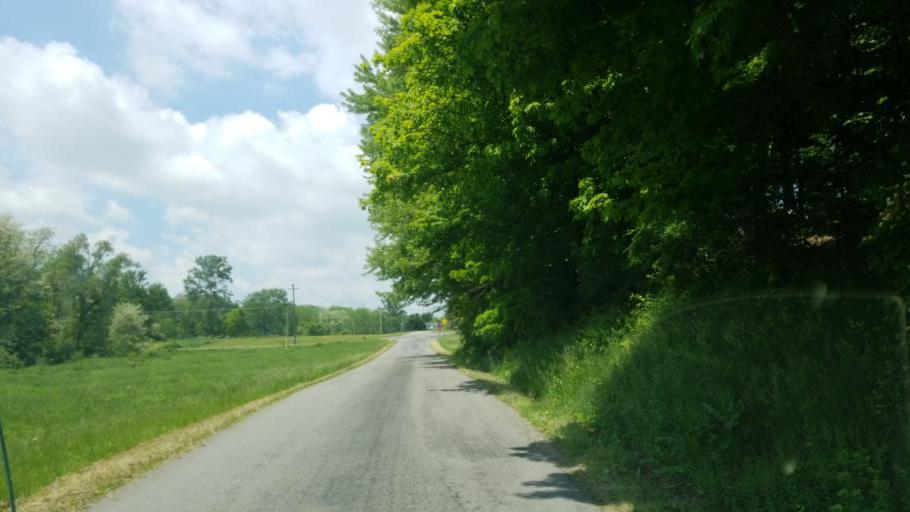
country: US
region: Ohio
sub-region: Ashland County
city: Ashland
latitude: 40.8407
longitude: -82.2776
